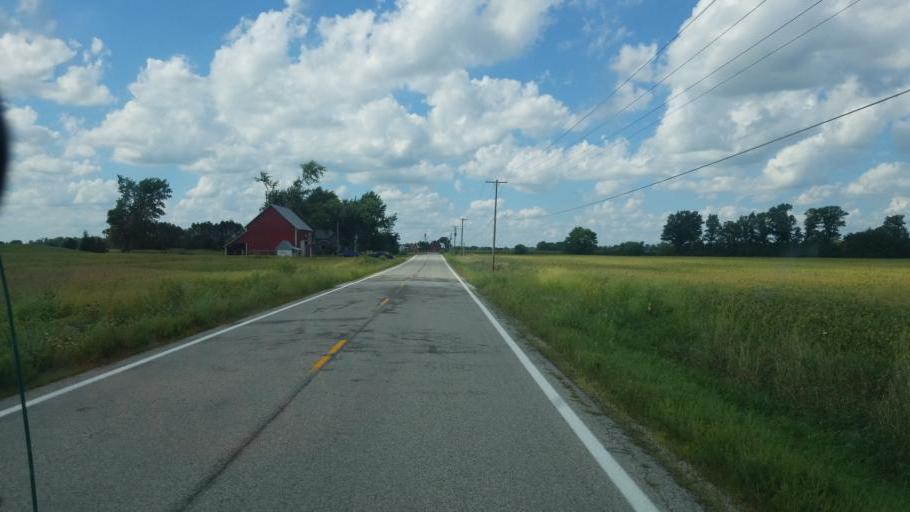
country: US
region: Ohio
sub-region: Union County
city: Richwood
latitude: 40.3775
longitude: -83.2745
